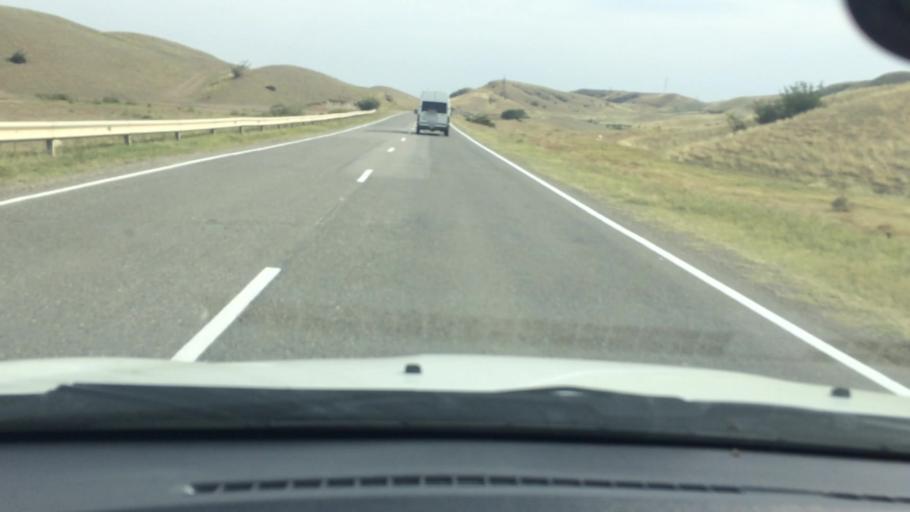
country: GE
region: Kvemo Kartli
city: Rust'avi
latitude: 41.5332
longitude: 44.9821
